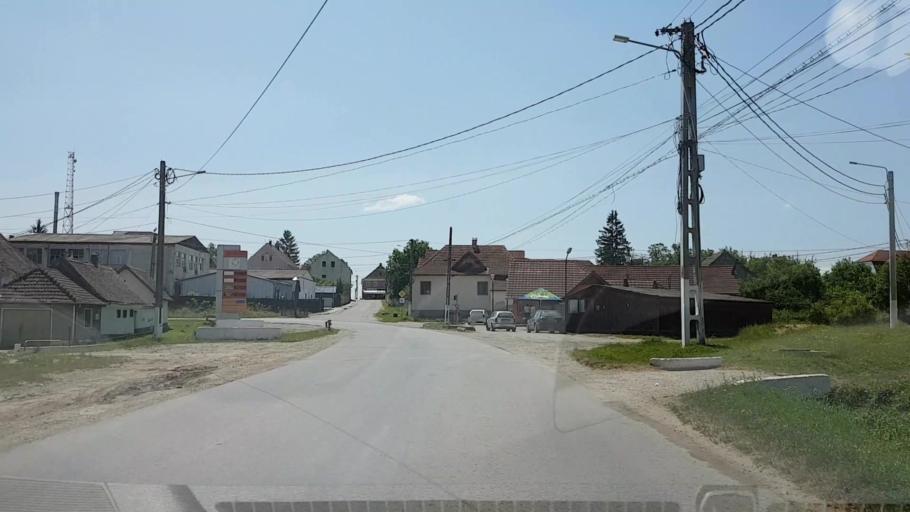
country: RO
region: Brasov
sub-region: Comuna Cincu
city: Cincu
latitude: 45.9175
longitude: 24.8013
